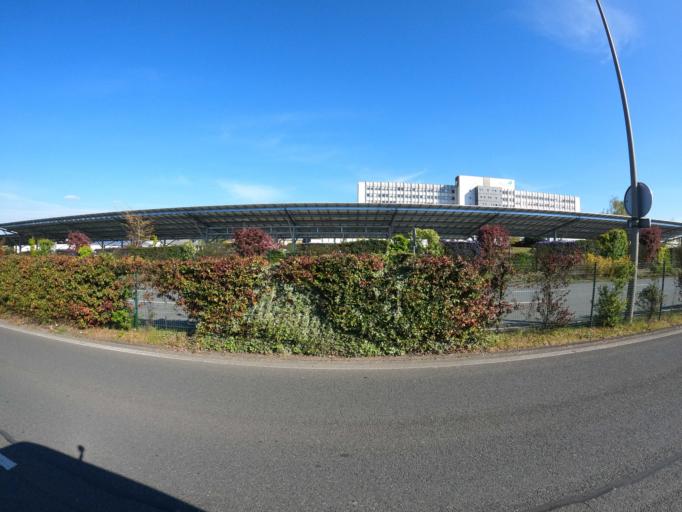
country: FR
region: Pays de la Loire
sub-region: Departement de Maine-et-Loire
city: Cholet
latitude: 47.0439
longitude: -0.8977
